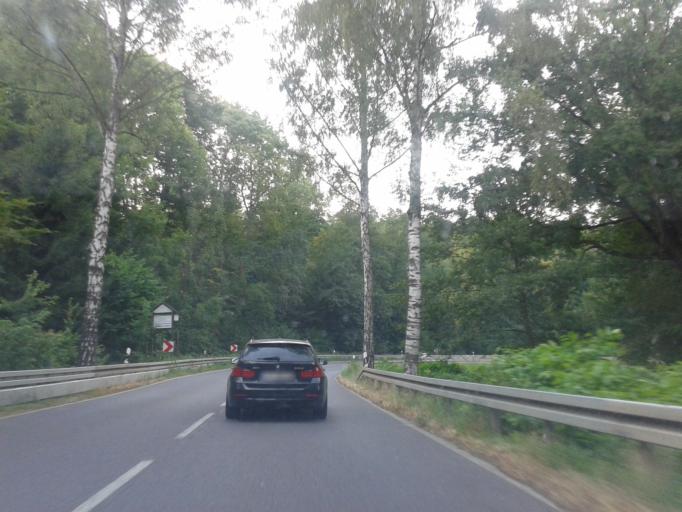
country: DE
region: Saxony
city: Niederschona
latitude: 51.0094
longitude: 13.4699
